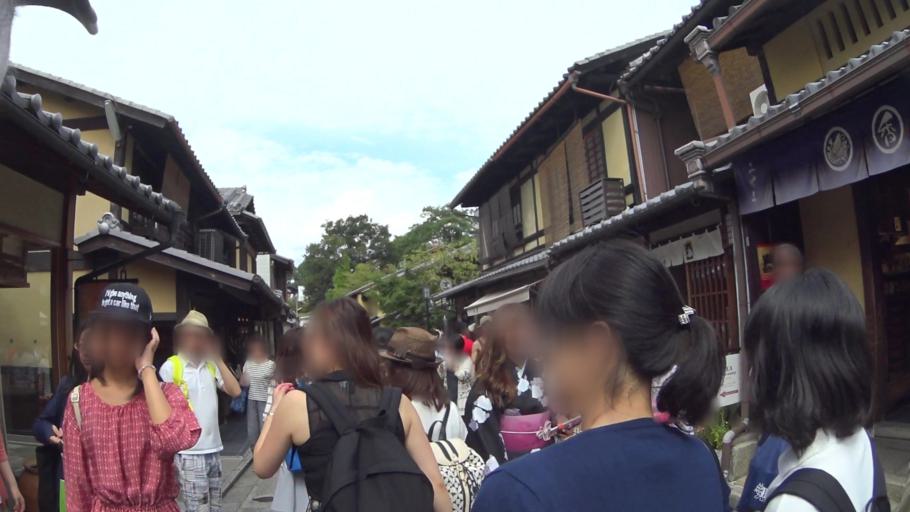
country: JP
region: Kyoto
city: Kyoto
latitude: 34.9986
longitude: 135.7808
